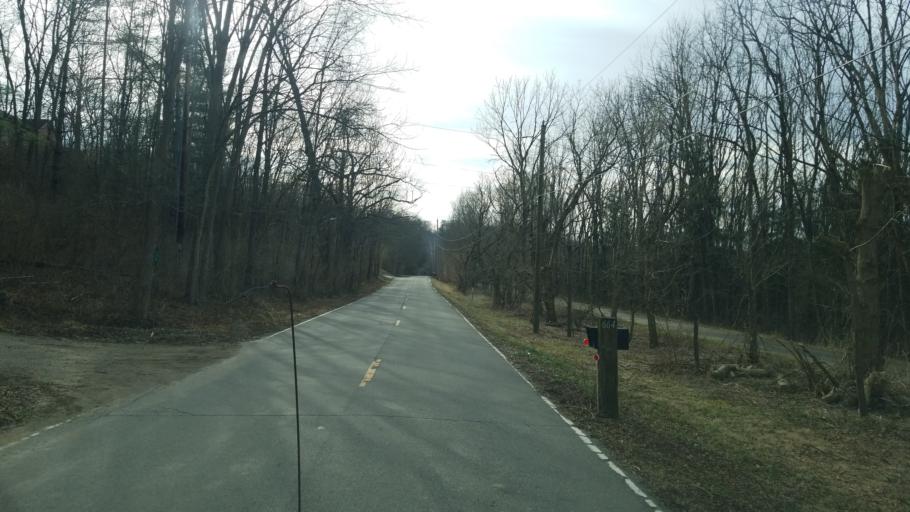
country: US
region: Ohio
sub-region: Warren County
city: Morrow
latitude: 39.4392
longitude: -84.1010
